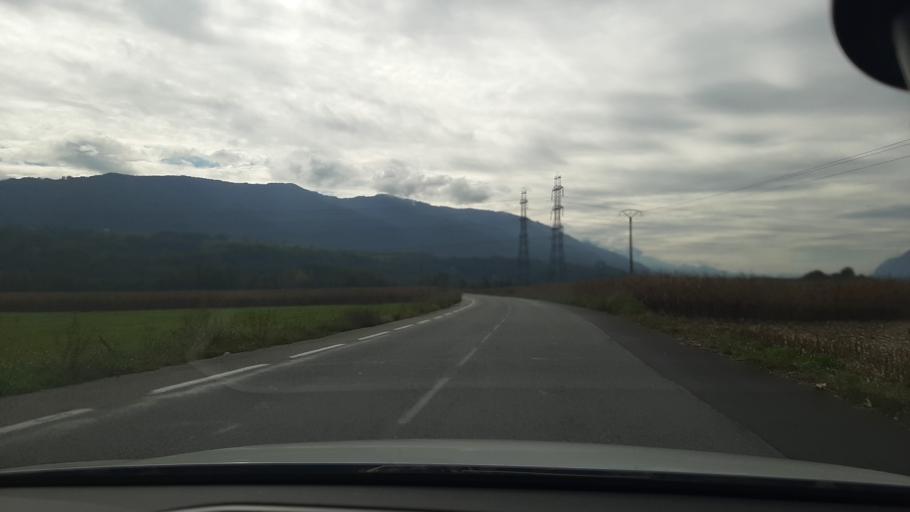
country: FR
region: Rhone-Alpes
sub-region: Departement de la Savoie
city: Montmelian
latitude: 45.4697
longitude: 6.0442
